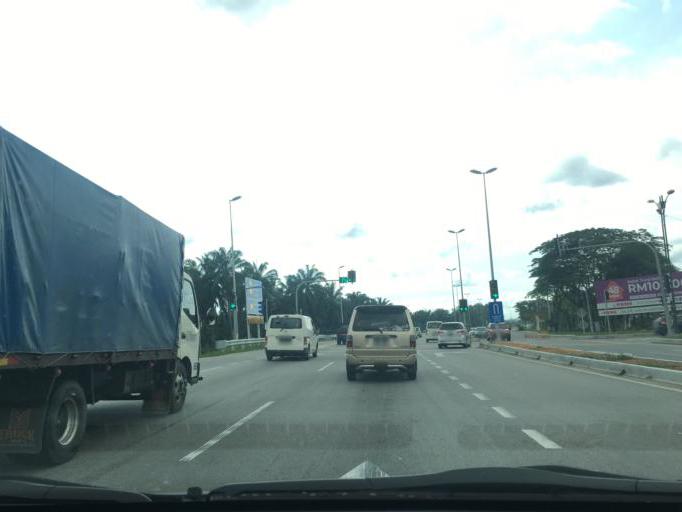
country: MY
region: Selangor
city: Batu Arang
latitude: 3.3031
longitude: 101.4320
